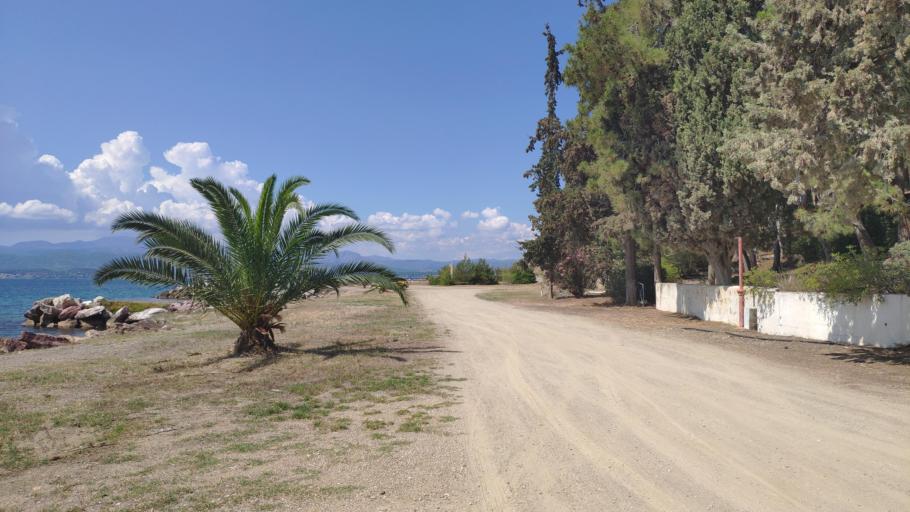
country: GR
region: Central Greece
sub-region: Nomos Evvoias
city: Eretria
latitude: 38.3844
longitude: 23.8009
